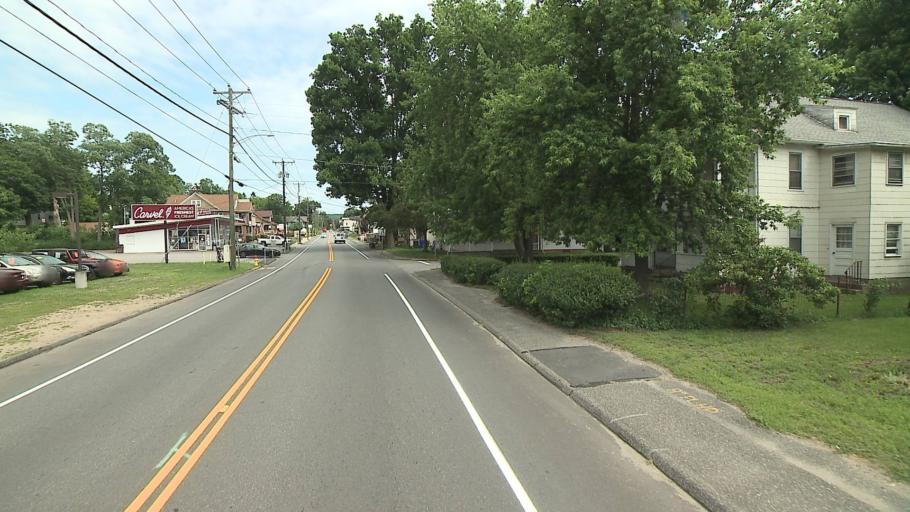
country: US
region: Connecticut
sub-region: Litchfield County
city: Torrington
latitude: 41.7868
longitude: -73.1176
